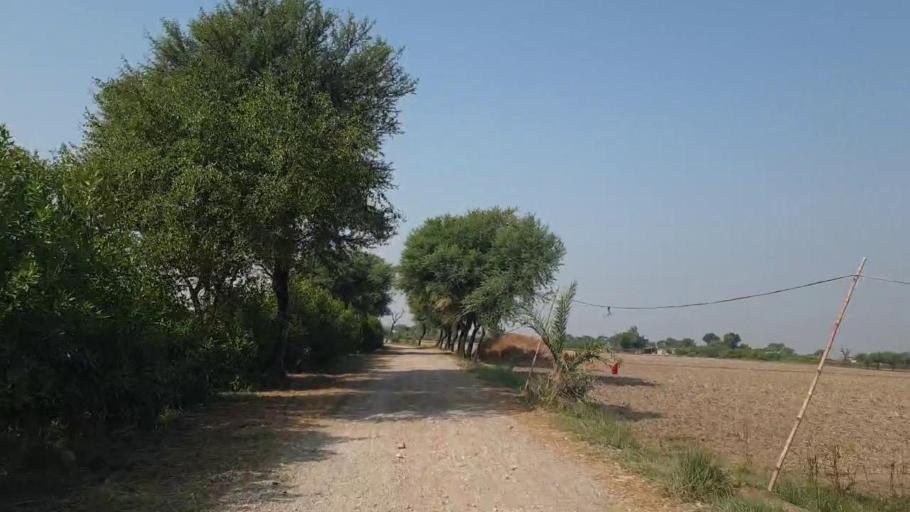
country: PK
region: Sindh
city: Matli
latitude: 24.9927
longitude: 68.6185
